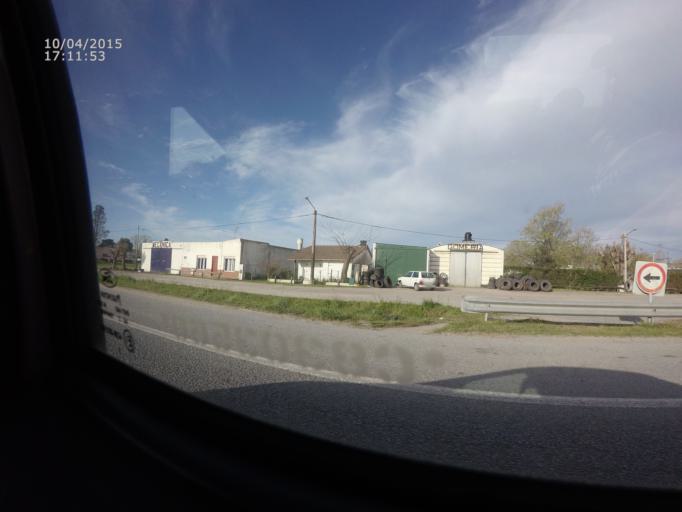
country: AR
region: Buenos Aires
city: Coronel Vidal
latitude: -37.2765
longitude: -57.7657
